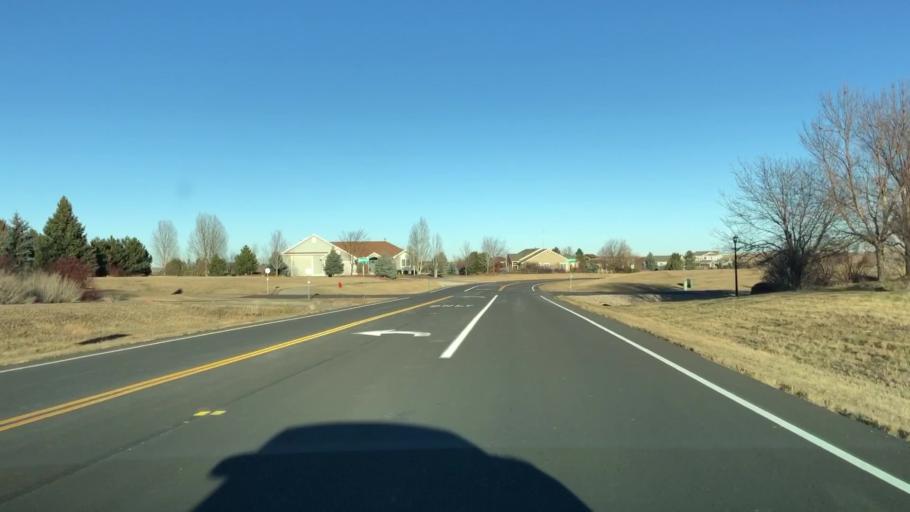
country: US
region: Colorado
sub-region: Weld County
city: Windsor
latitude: 40.4451
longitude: -104.9515
